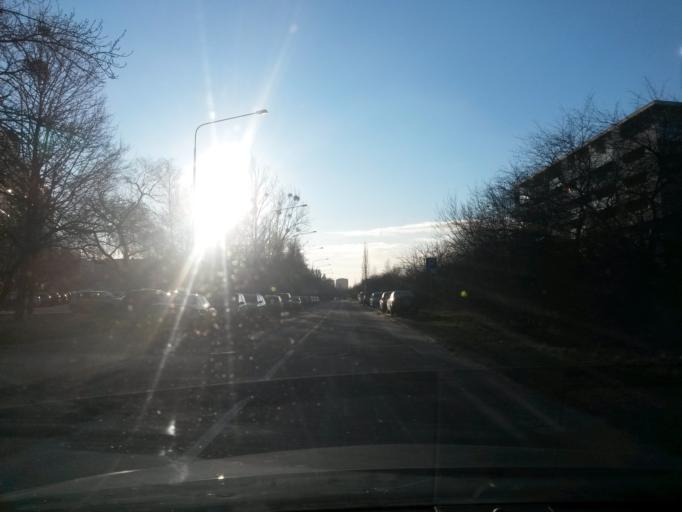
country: PL
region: Greater Poland Voivodeship
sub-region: Poznan
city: Poznan
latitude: 52.3922
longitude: 16.9702
